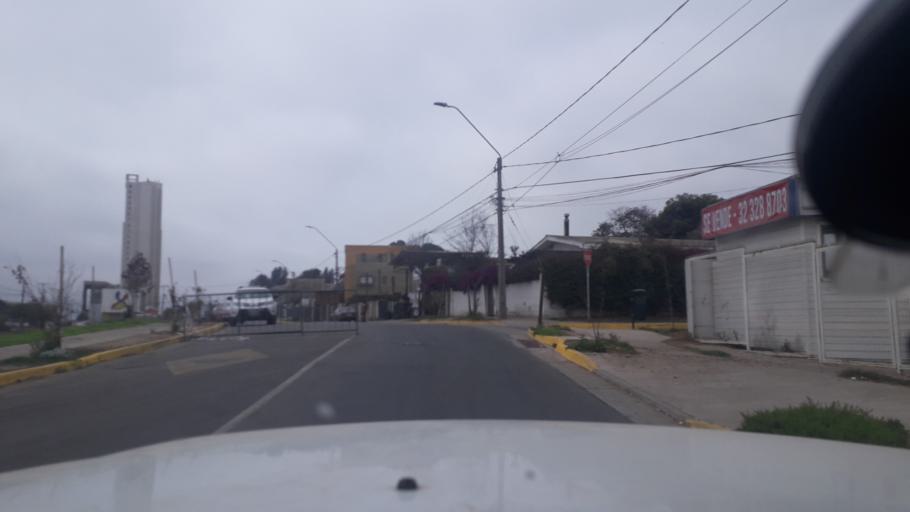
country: CL
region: Valparaiso
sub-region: Provincia de Valparaiso
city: Vina del Mar
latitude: -32.9336
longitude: -71.5245
